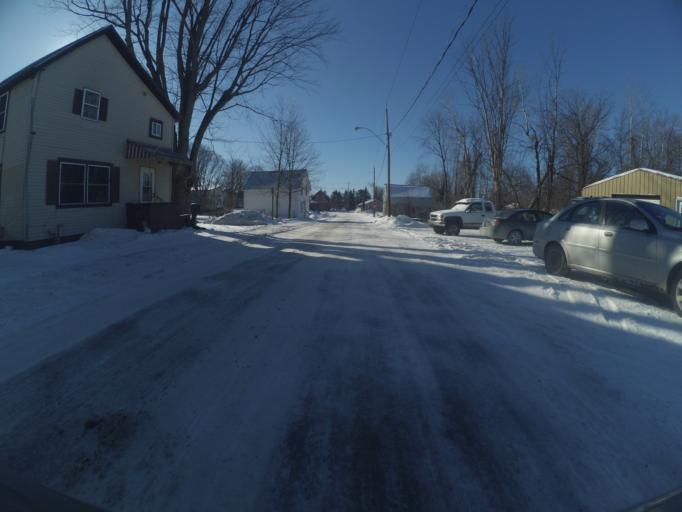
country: US
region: New York
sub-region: St. Lawrence County
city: Potsdam
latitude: 44.6738
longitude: -74.9896
